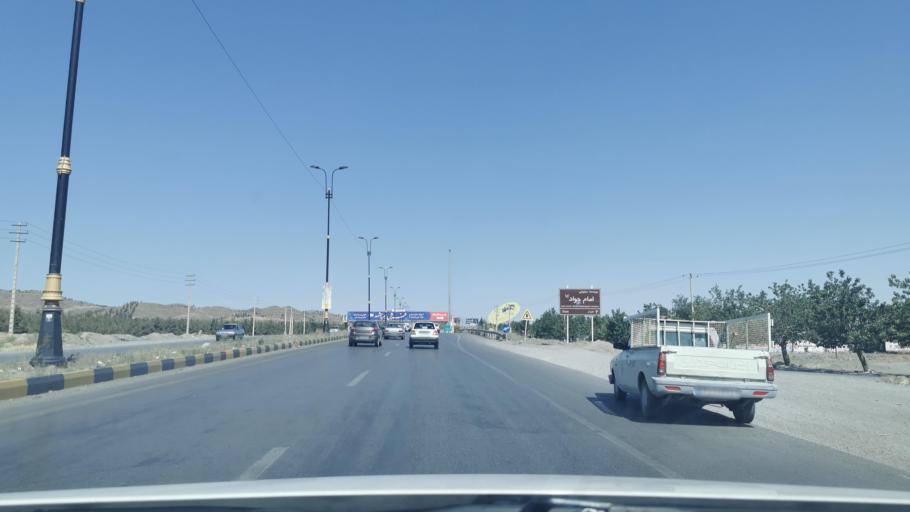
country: IR
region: Razavi Khorasan
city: Torqabeh
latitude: 36.4032
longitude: 59.3844
